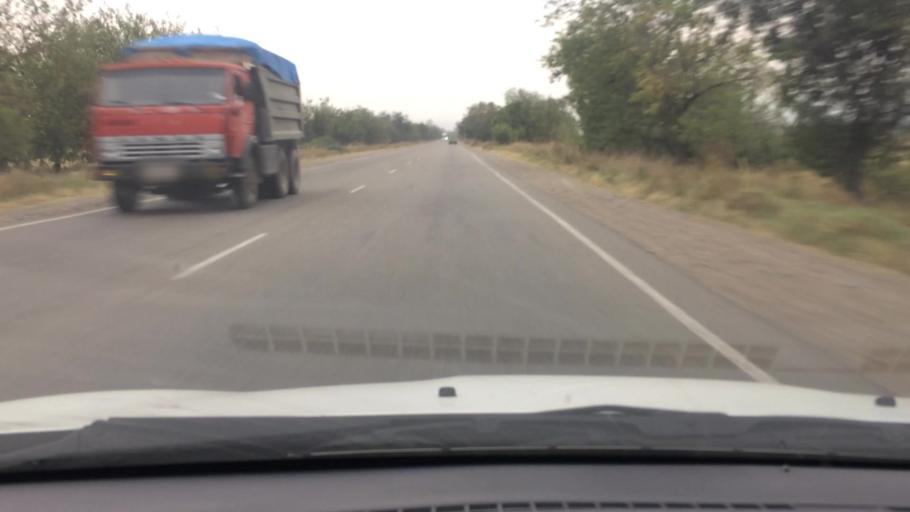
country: GE
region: Kvemo Kartli
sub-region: Marneuli
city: Marneuli
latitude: 41.5647
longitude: 44.7755
